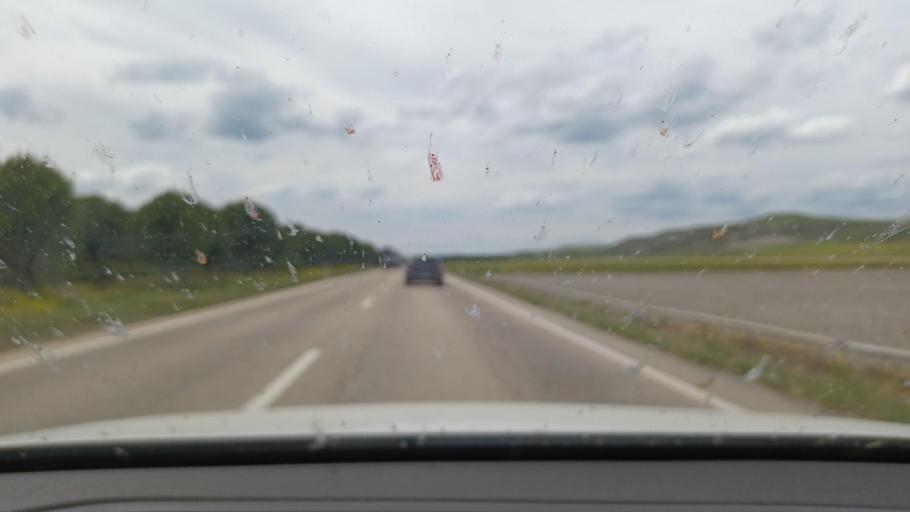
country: ES
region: Castille and Leon
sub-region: Provincia de Segovia
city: Frumales
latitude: 41.3823
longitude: -4.2148
